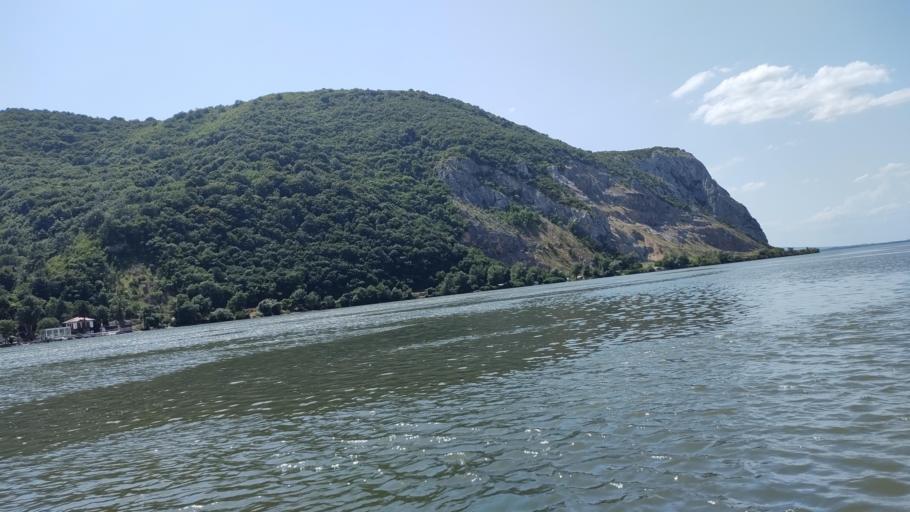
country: RO
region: Caras-Severin
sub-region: Comuna Pescari
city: Coronini
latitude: 44.6571
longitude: 21.7113
